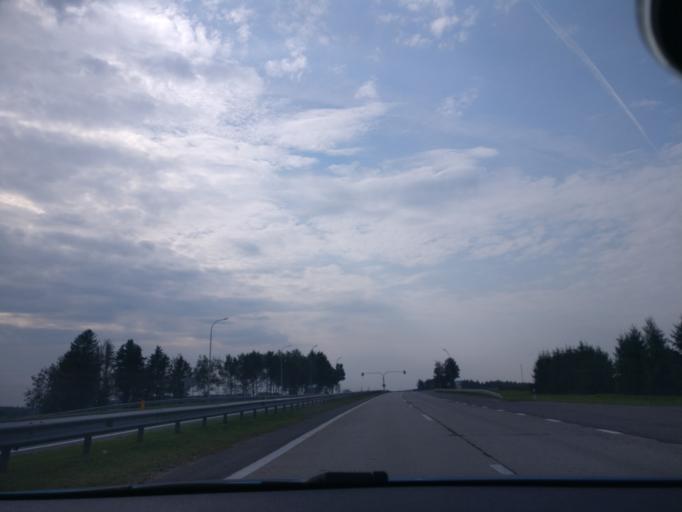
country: BY
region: Minsk
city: Lahoysk
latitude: 54.1665
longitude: 27.8176
